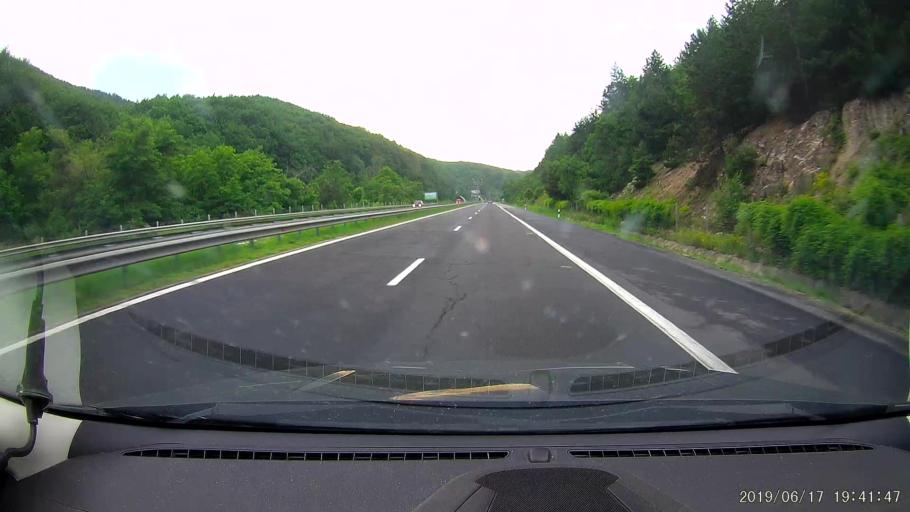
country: BG
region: Sofiya
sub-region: Obshtina Ikhtiman
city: Ikhtiman
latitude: 42.3495
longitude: 23.9275
